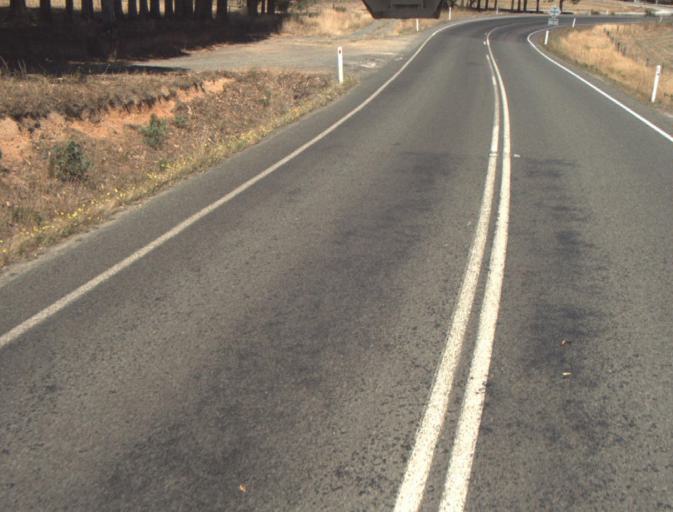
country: AU
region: Tasmania
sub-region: Launceston
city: Newstead
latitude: -41.3290
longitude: 147.3537
